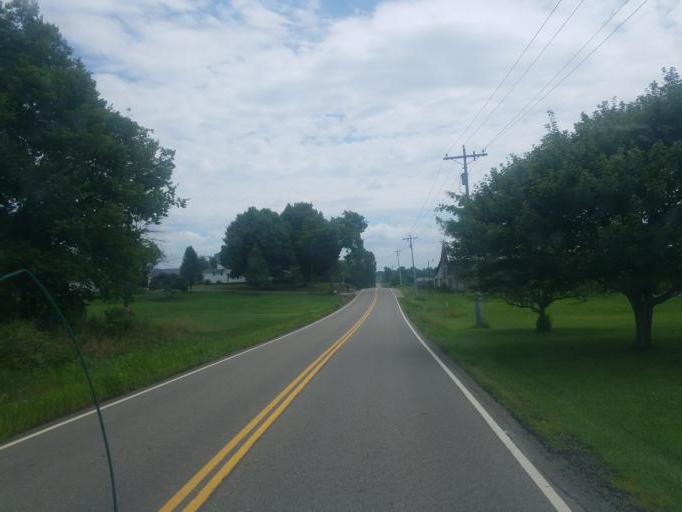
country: US
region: Ohio
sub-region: Knox County
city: Centerburg
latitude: 40.2498
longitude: -82.5872
